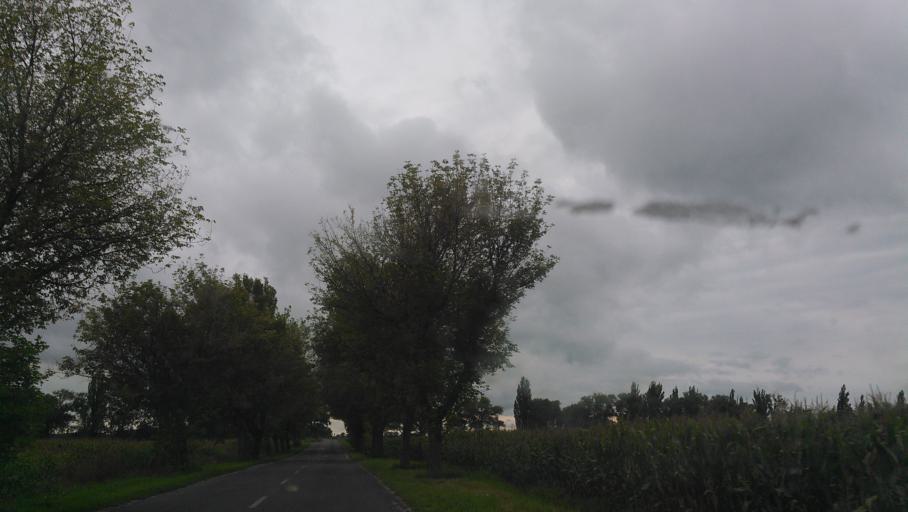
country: SK
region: Trnavsky
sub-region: Okres Dunajska Streda
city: Velky Meder
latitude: 47.9071
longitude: 17.7775
